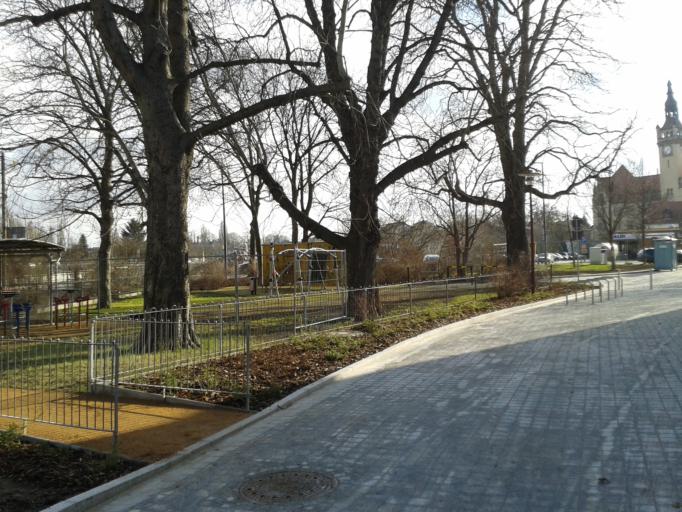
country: DE
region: Saxony
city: Dresden
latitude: 51.0582
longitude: 13.6879
